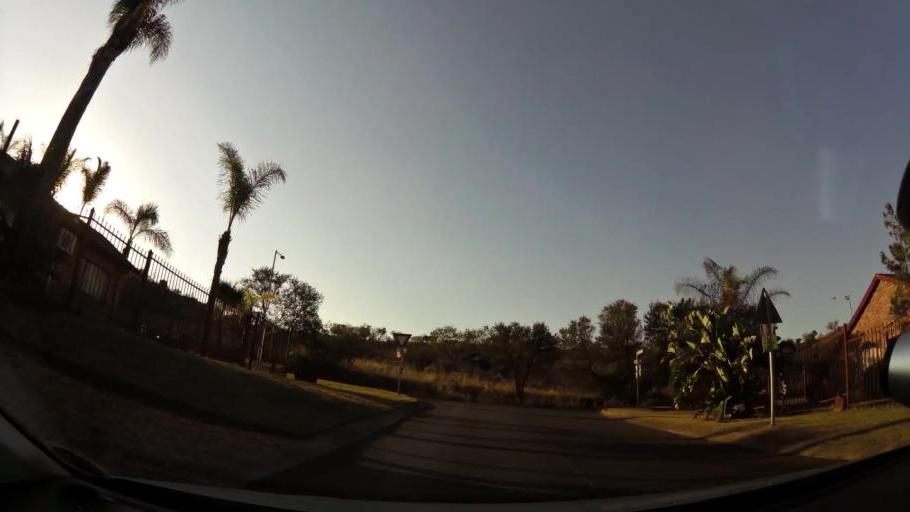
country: ZA
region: Gauteng
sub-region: City of Tshwane Metropolitan Municipality
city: Pretoria
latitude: -25.7314
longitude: 28.1298
